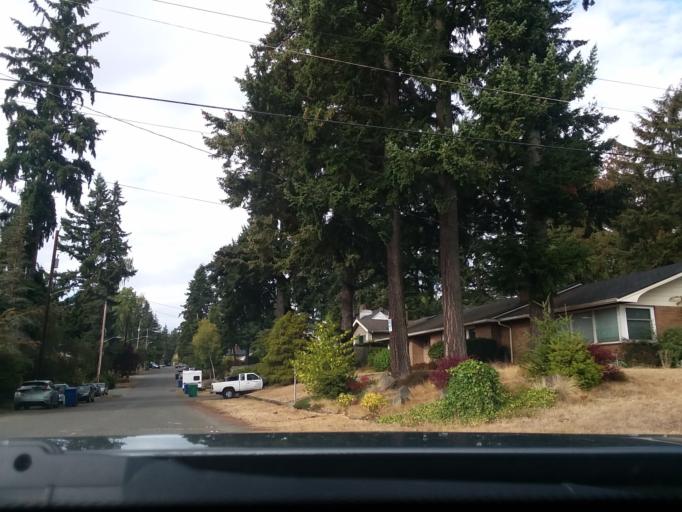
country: US
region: Washington
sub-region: King County
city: Shoreline
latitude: 47.7215
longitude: -122.3623
